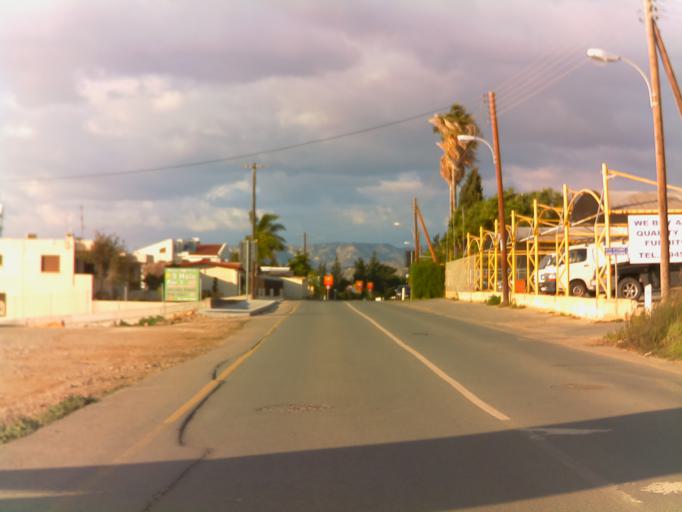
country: CY
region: Pafos
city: Chlorakas
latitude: 34.8063
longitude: 32.4105
